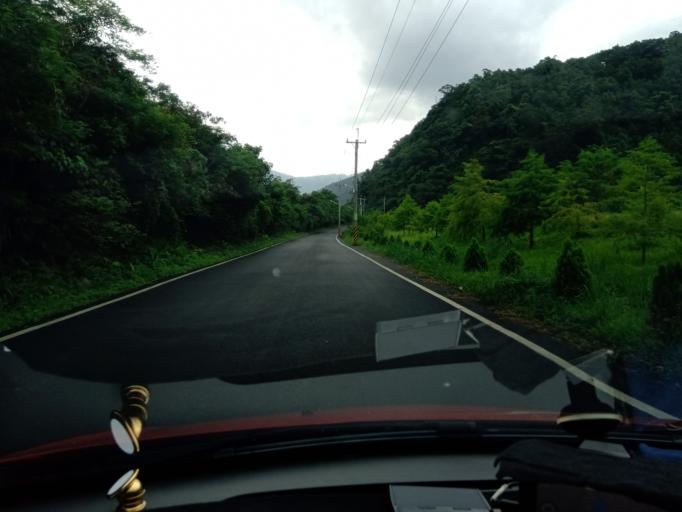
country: TW
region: Taiwan
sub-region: Yilan
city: Yilan
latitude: 24.7813
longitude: 121.7083
